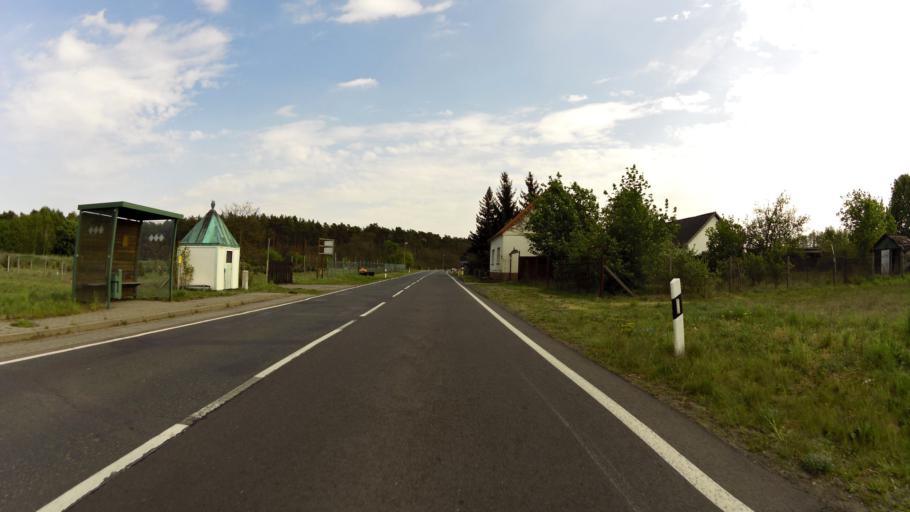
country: DE
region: Brandenburg
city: Spreenhagen
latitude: 52.3351
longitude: 13.8948
